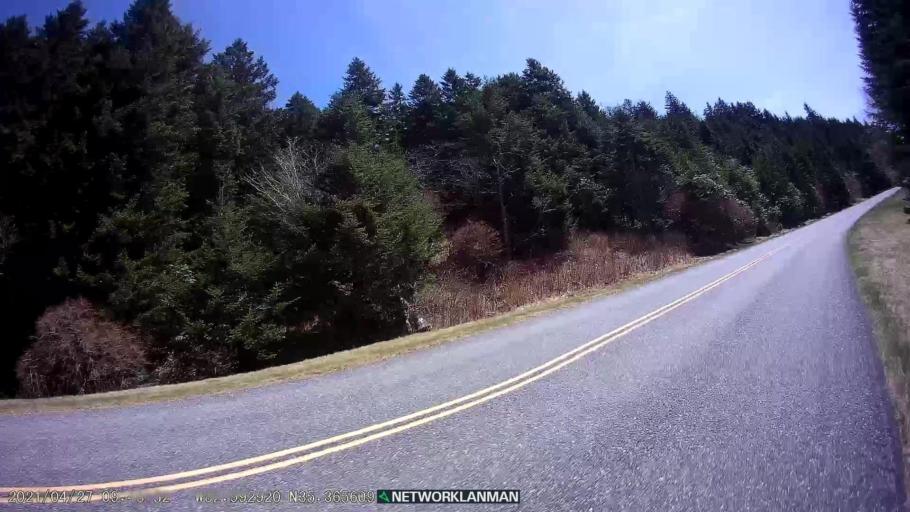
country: US
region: North Carolina
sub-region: Haywood County
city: Hazelwood
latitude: 35.3655
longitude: -82.9928
